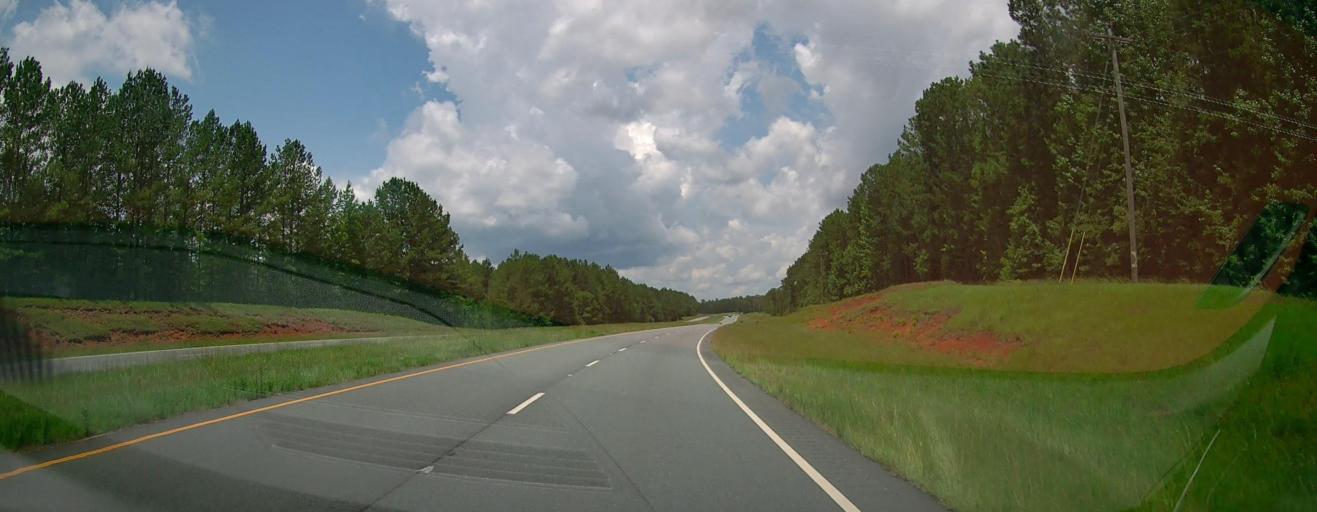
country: US
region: Georgia
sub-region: Upson County
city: Thomaston
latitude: 32.7984
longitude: -84.2722
